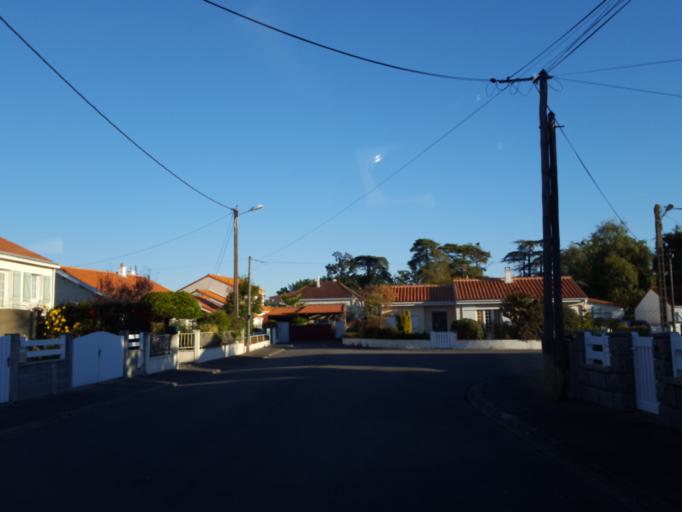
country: FR
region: Pays de la Loire
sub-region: Departement de la Loire-Atlantique
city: Basse-Goulaine
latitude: 47.2119
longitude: -1.4691
